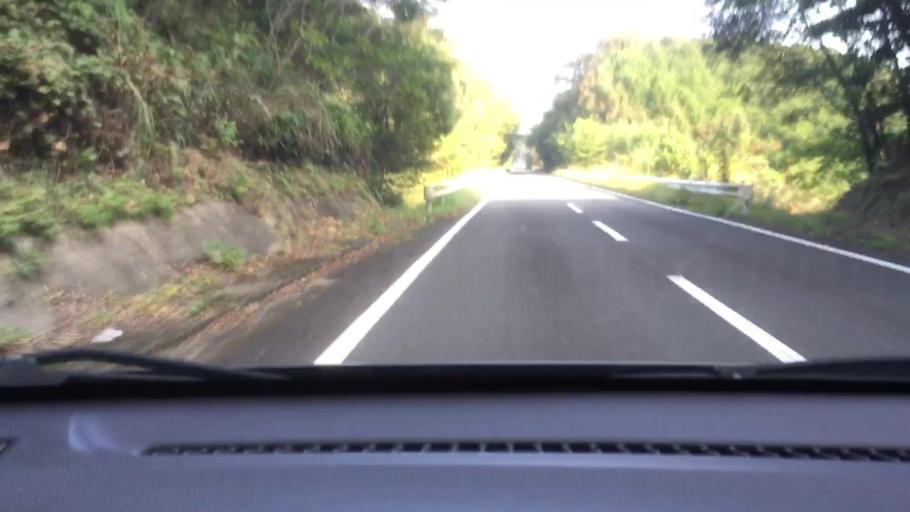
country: JP
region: Nagasaki
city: Sasebo
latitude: 33.0003
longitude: 129.7074
